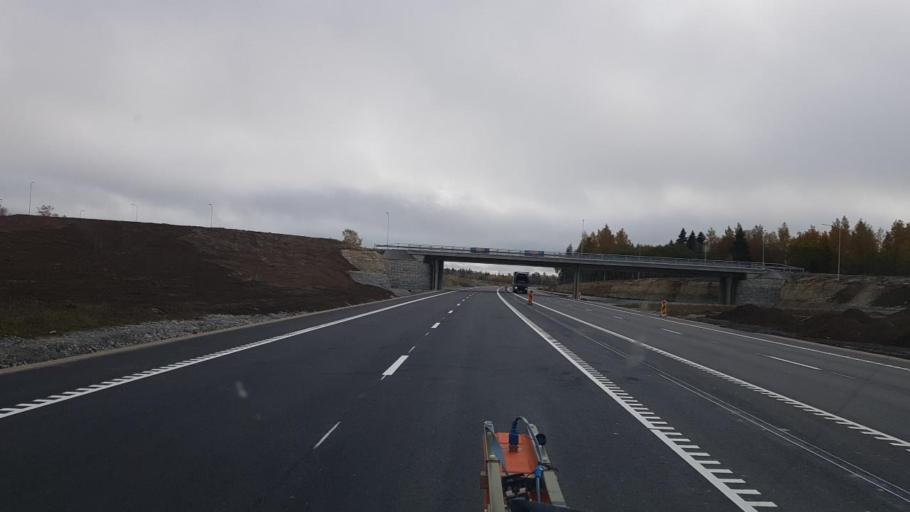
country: EE
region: Jaervamaa
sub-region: Paide linn
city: Paide
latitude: 58.9938
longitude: 25.5880
